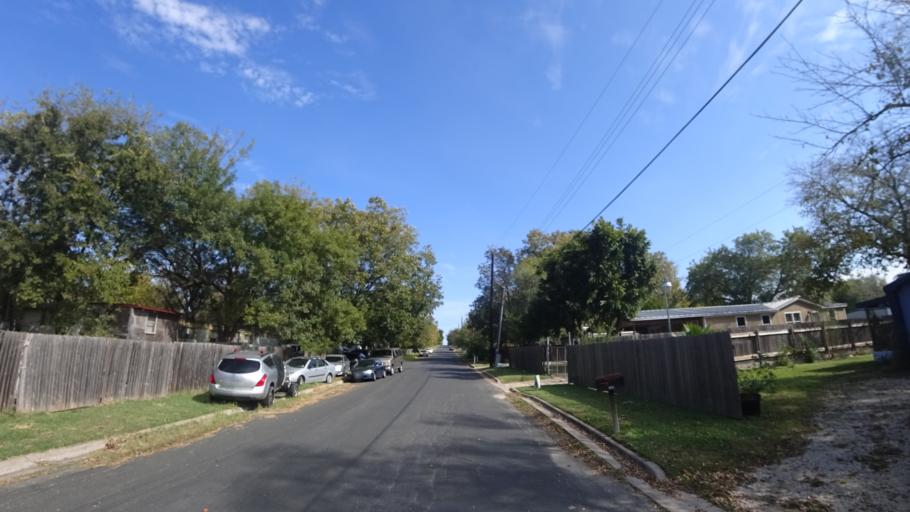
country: US
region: Texas
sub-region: Travis County
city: Pflugerville
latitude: 30.4086
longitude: -97.6340
